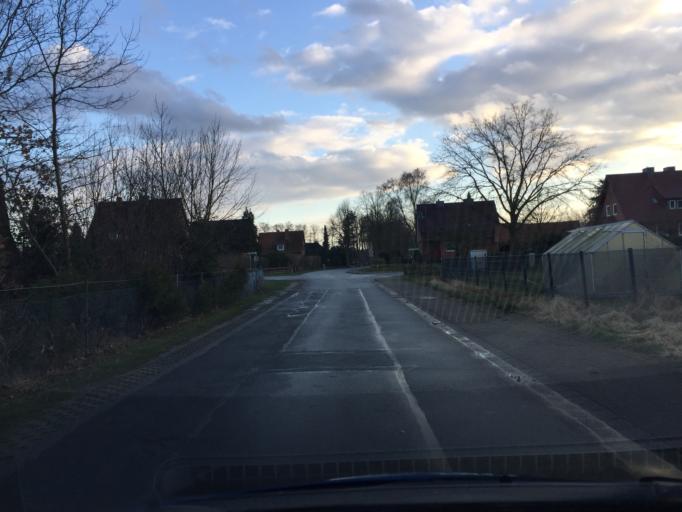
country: DE
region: Lower Saxony
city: Echem
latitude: 53.3370
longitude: 10.5432
